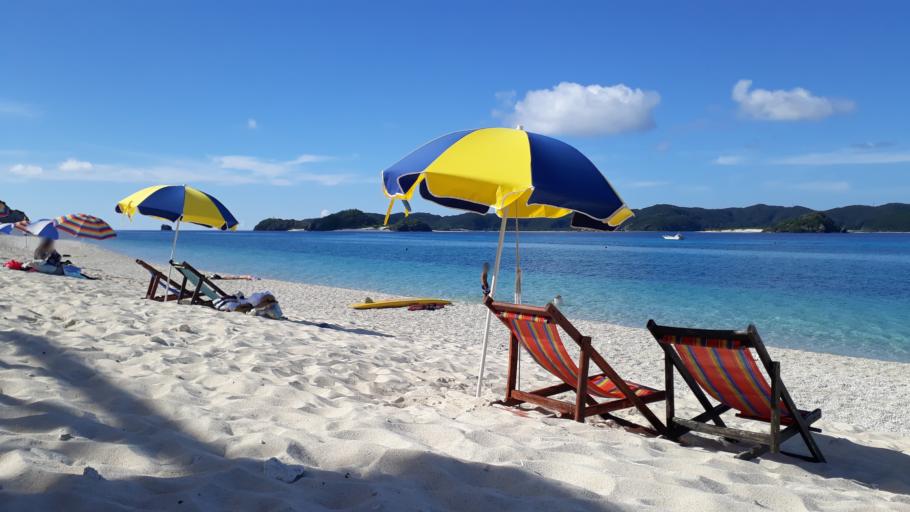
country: JP
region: Okinawa
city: Okinawa
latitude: 26.3344
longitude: 127.7917
